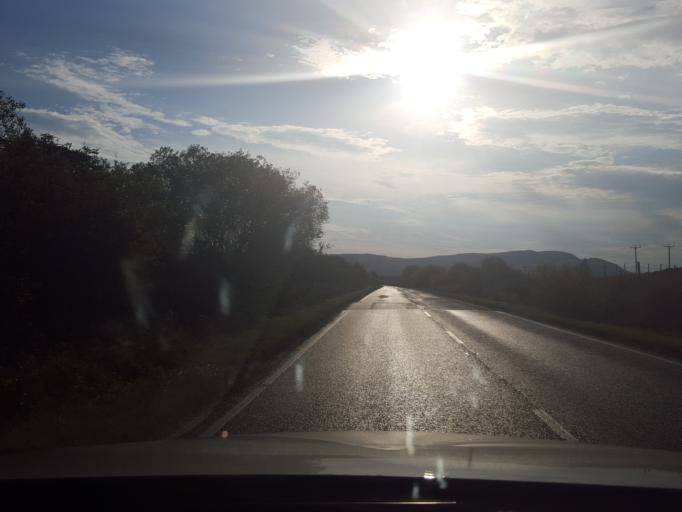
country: GB
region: Scotland
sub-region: Highland
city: Portree
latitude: 57.2553
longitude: -5.9390
